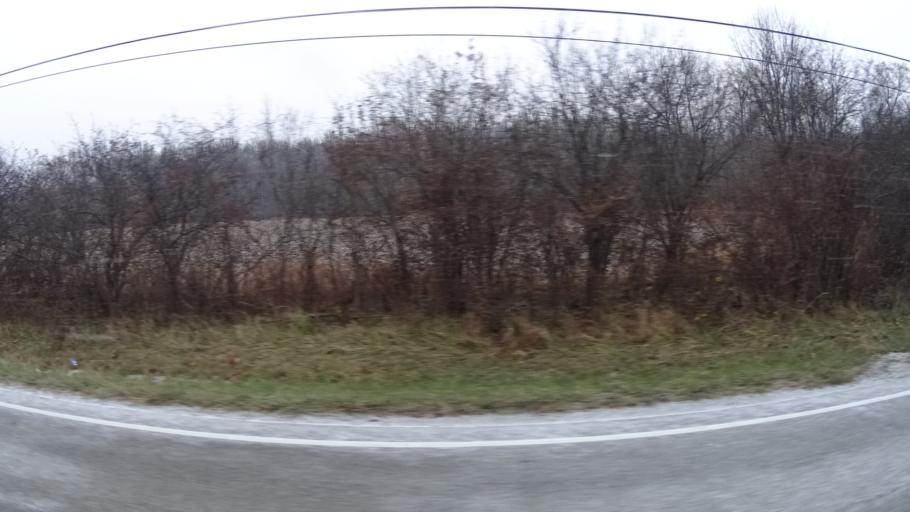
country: US
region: Ohio
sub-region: Lorain County
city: Oberlin
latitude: 41.3089
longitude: -82.2291
